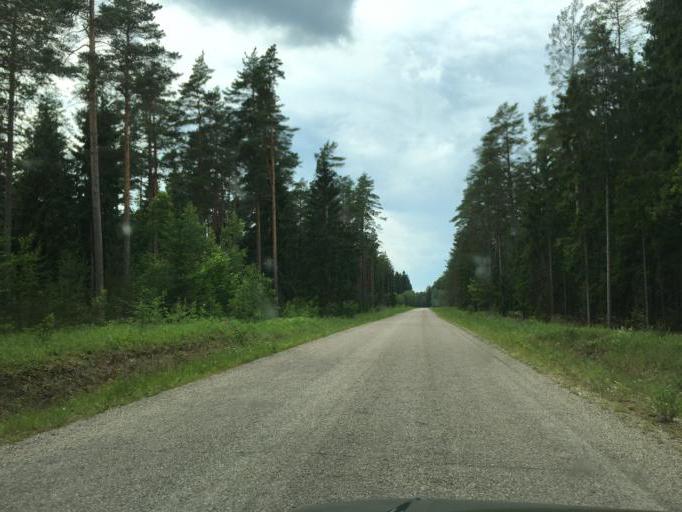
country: LV
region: Vilanu
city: Vilani
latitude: 56.7419
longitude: 27.0519
